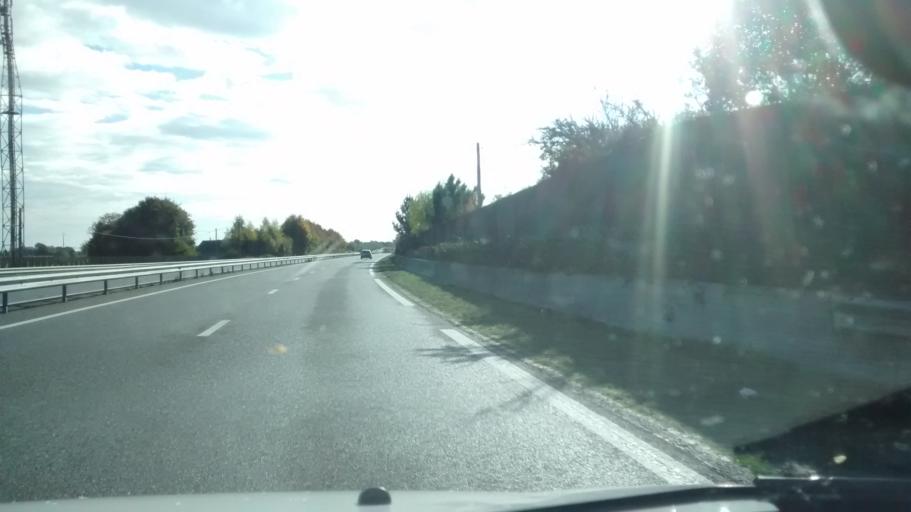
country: FR
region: Brittany
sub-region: Departement d'Ille-et-Vilaine
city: Corps-Nuds
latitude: 47.9848
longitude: -1.5710
